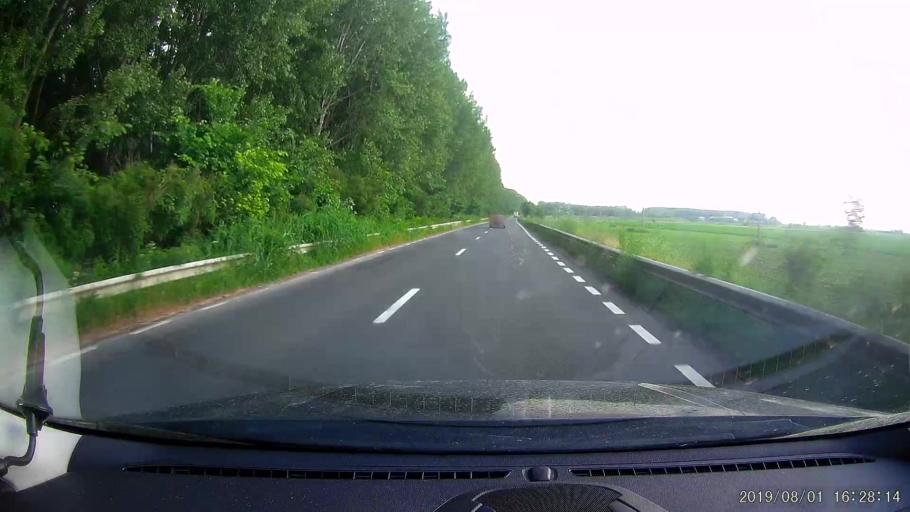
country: RO
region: Calarasi
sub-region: Municipiul Calarasi
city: Calarasi
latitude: 44.1506
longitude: 27.3116
